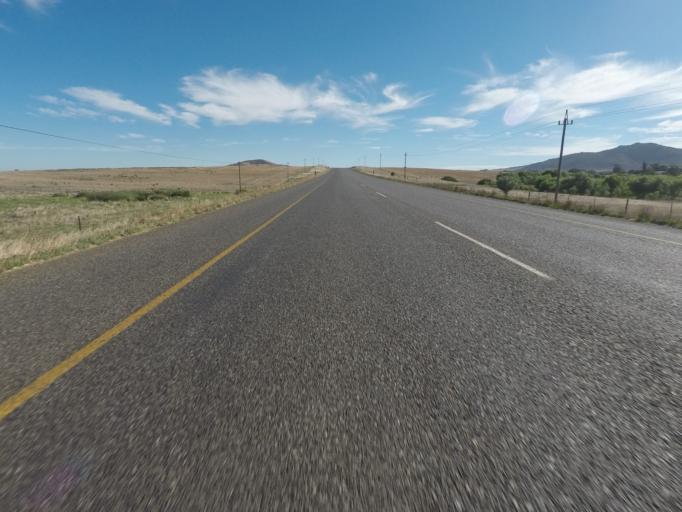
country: ZA
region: Western Cape
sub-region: West Coast District Municipality
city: Malmesbury
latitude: -33.6136
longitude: 18.7272
